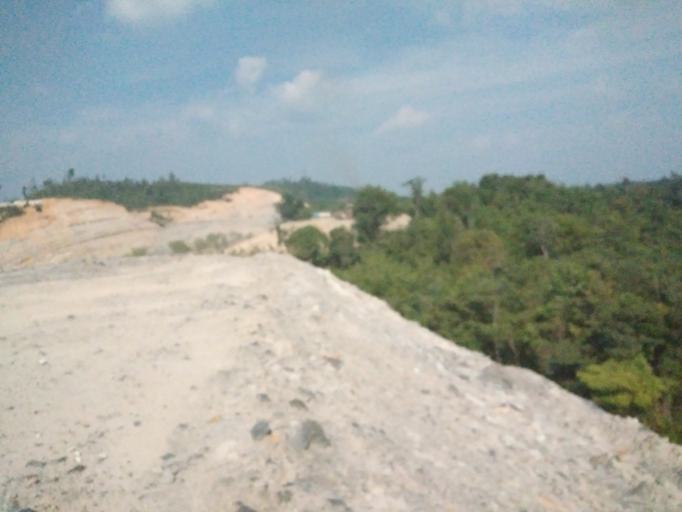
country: ID
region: Jambi
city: Muara Tebo
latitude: -1.2777
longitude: 102.5512
